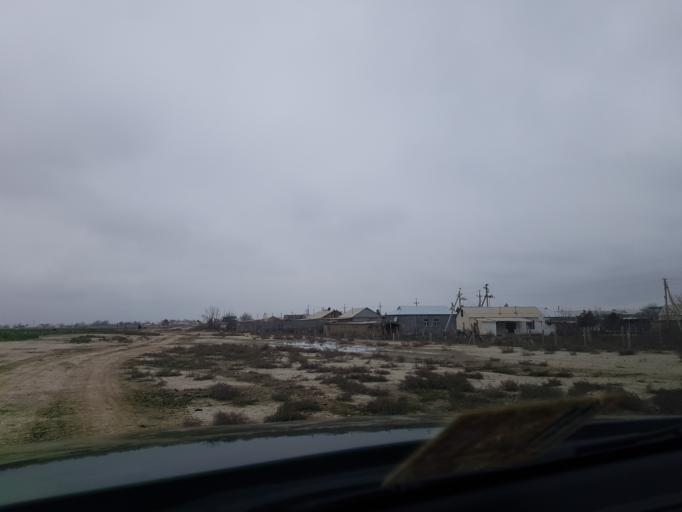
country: TM
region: Ahal
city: Abadan
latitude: 38.1404
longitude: 57.9694
